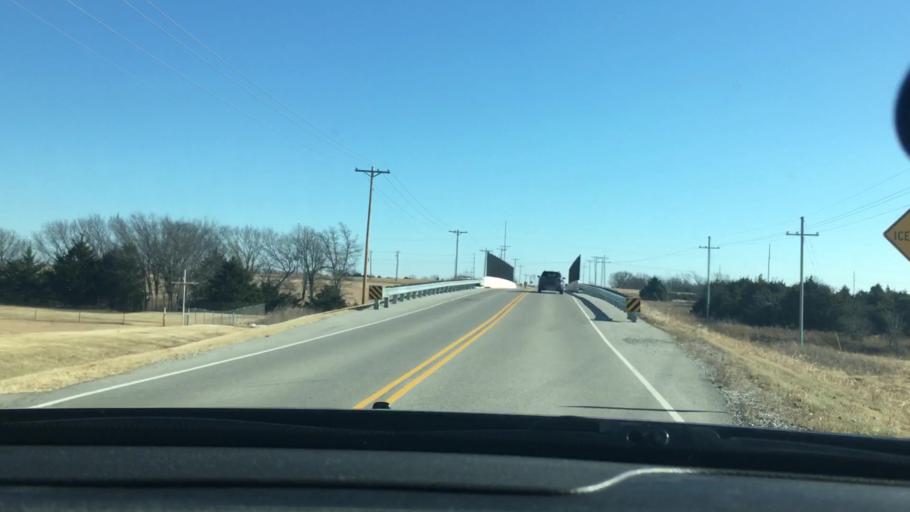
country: US
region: Oklahoma
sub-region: Murray County
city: Davis
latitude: 34.4774
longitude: -97.1114
